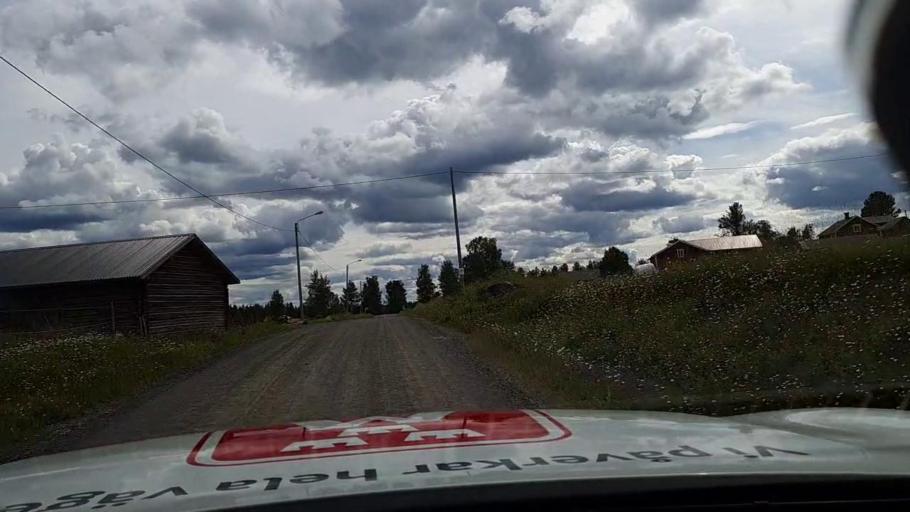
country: SE
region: Jaemtland
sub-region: Braecke Kommun
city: Braecke
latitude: 63.2836
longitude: 15.3706
